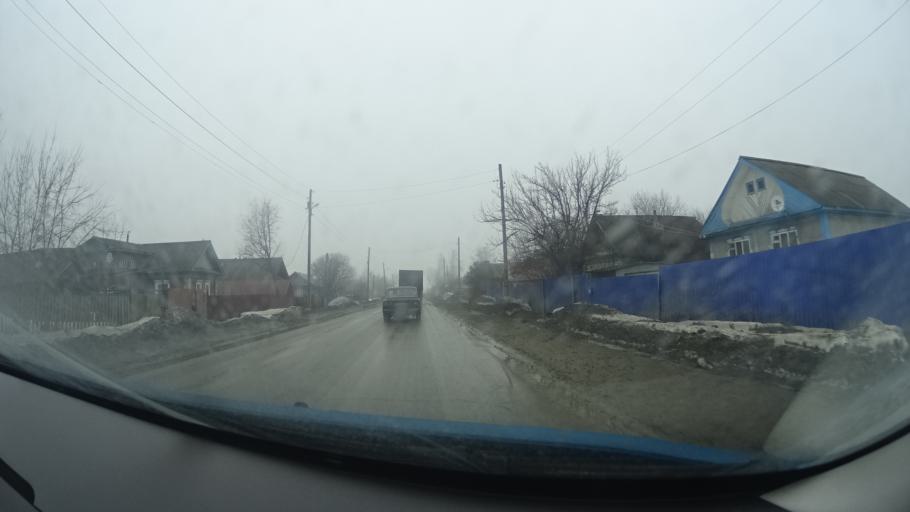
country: RU
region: Perm
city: Kuyeda
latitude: 56.4289
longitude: 55.5790
